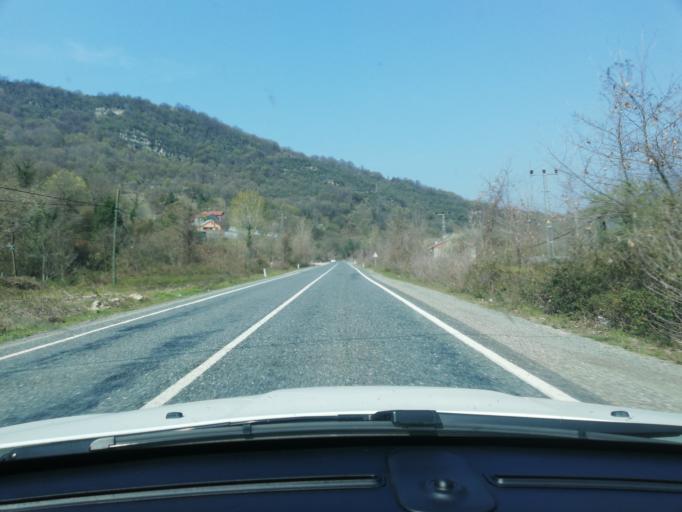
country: TR
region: Zonguldak
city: Gokcebey
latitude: 41.2240
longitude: 32.2194
